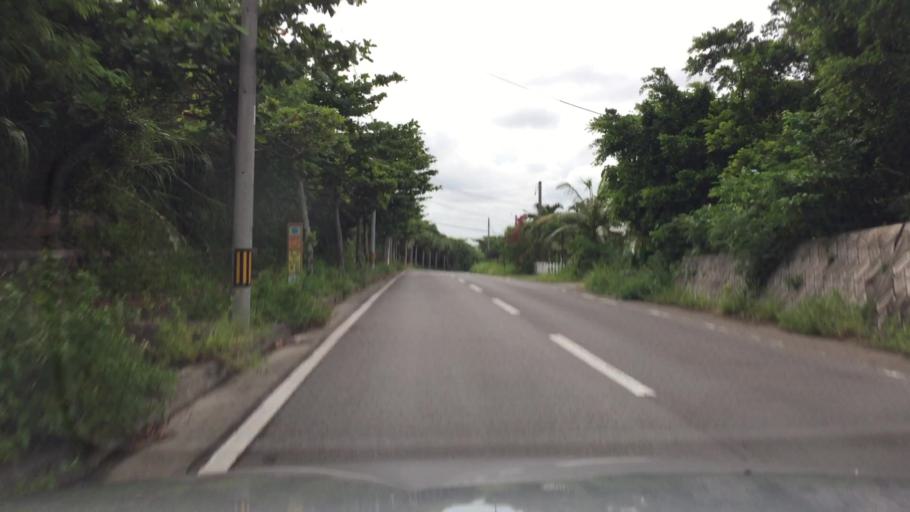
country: JP
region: Okinawa
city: Ishigaki
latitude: 24.4463
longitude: 124.1718
